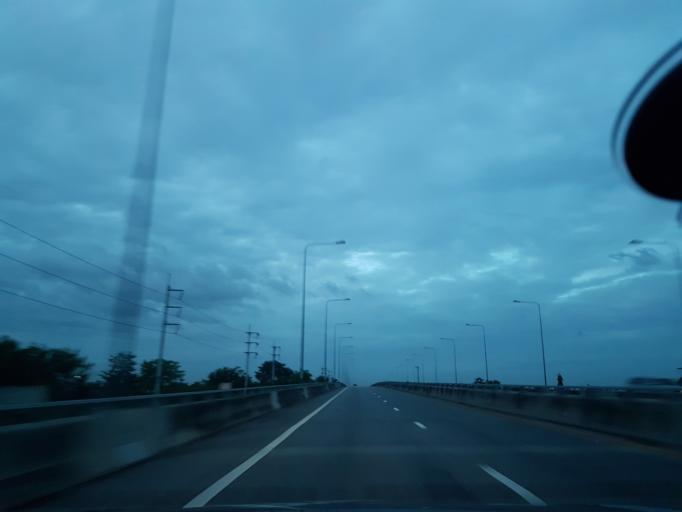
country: TH
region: Pathum Thani
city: Sam Khok
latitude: 14.0831
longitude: 100.5788
